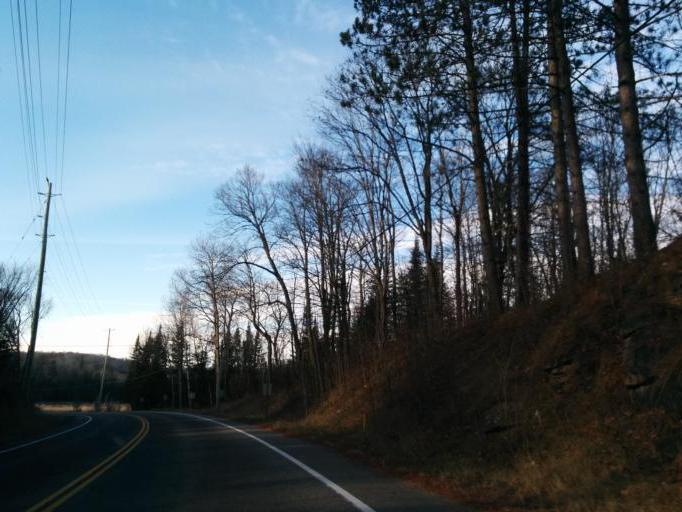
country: CA
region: Ontario
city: Bancroft
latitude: 45.0251
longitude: -78.3824
